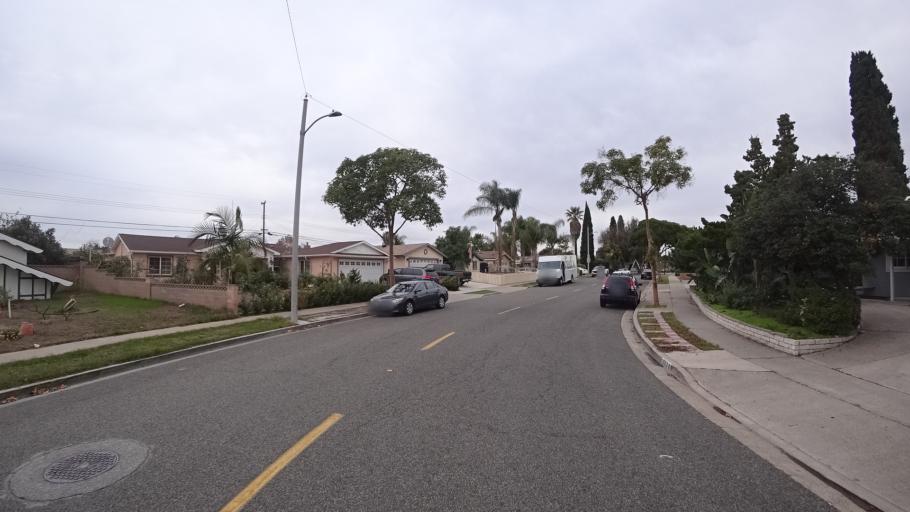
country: US
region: California
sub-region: Orange County
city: Garden Grove
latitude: 33.7796
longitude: -117.9245
